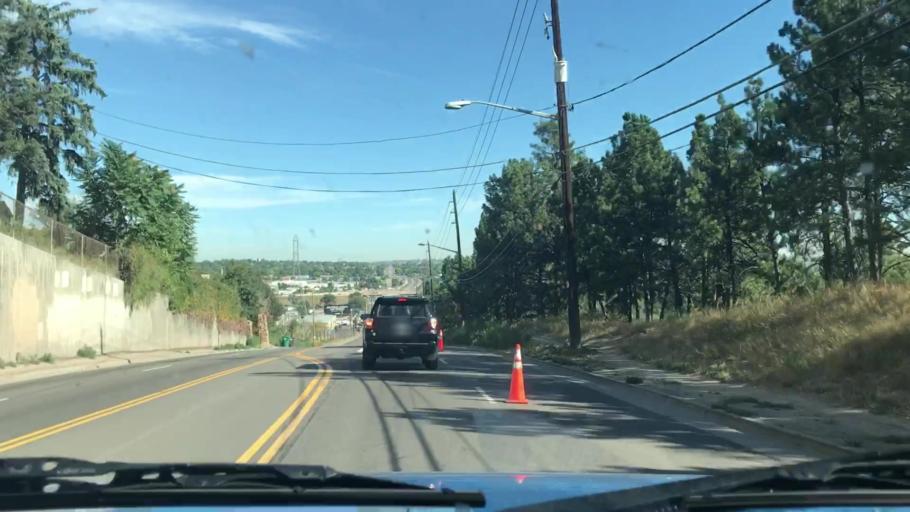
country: US
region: Colorado
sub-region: Adams County
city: Berkley
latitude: 39.7881
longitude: -105.0533
